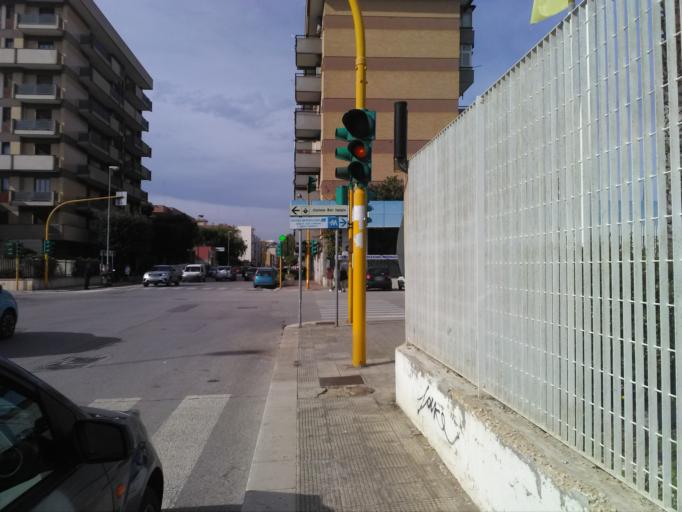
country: IT
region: Apulia
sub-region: Provincia di Bari
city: Bari
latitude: 41.1134
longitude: 16.8978
